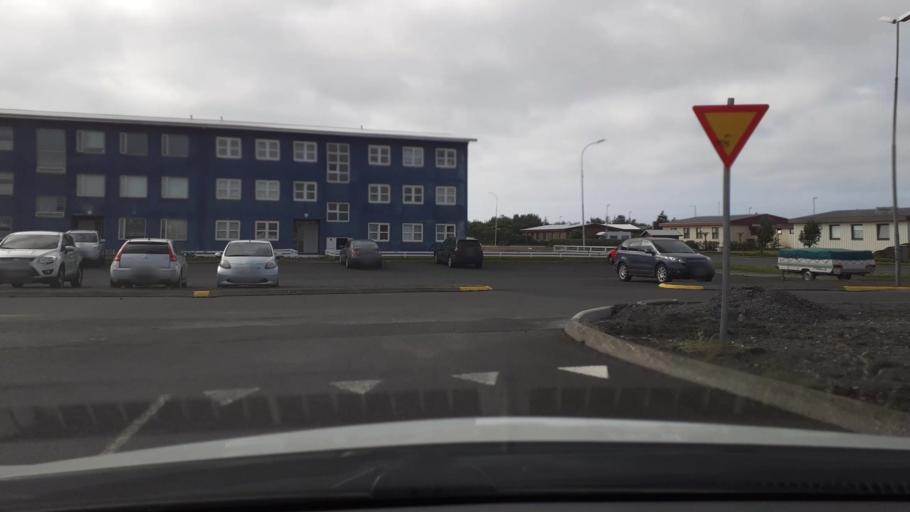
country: IS
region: South
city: THorlakshoefn
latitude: 63.8576
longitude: -21.3911
